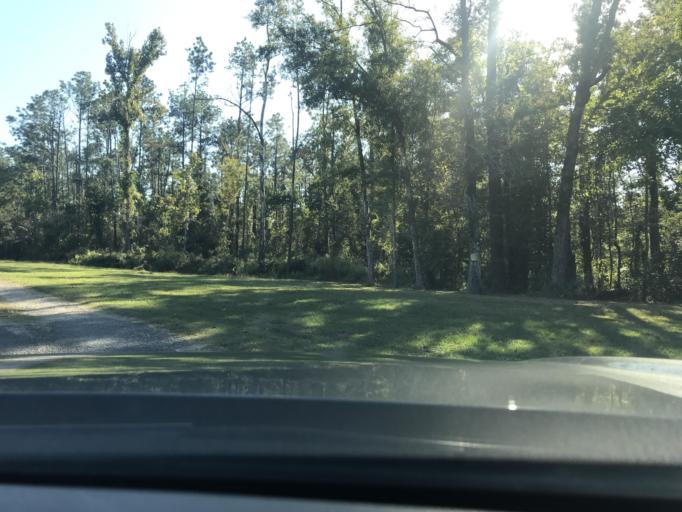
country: US
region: Louisiana
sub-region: Calcasieu Parish
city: Westlake
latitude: 30.3153
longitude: -93.2753
